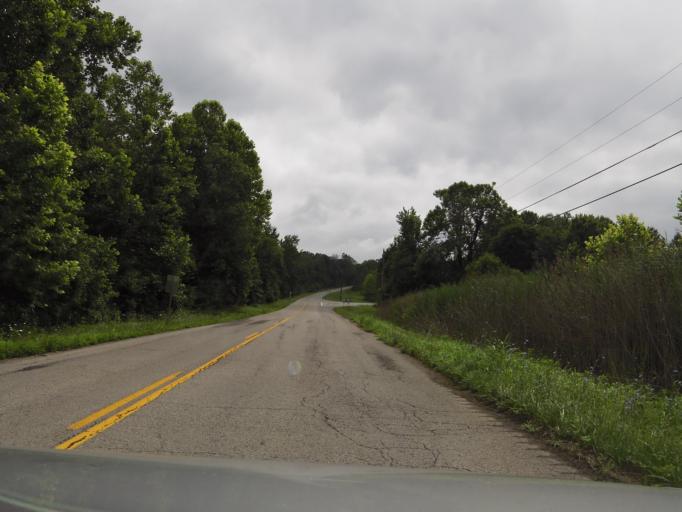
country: US
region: Kentucky
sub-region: Muhlenberg County
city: Morehead
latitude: 37.3027
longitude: -87.3228
